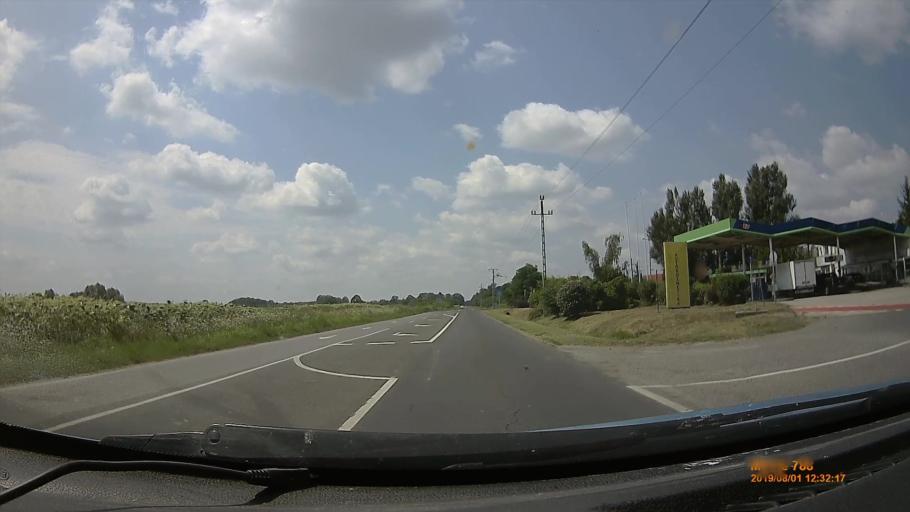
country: HU
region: Baranya
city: Siklos
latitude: 45.8561
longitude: 18.2685
